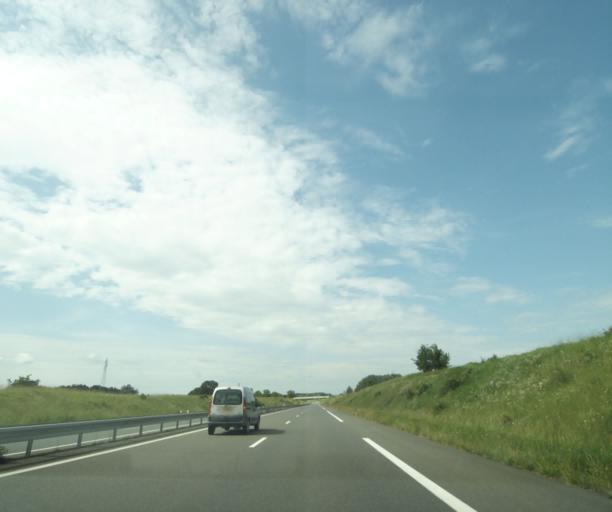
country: FR
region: Pays de la Loire
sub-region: Departement de Maine-et-Loire
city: Saint-Philbert-du-Peuple
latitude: 47.3668
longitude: -0.0836
